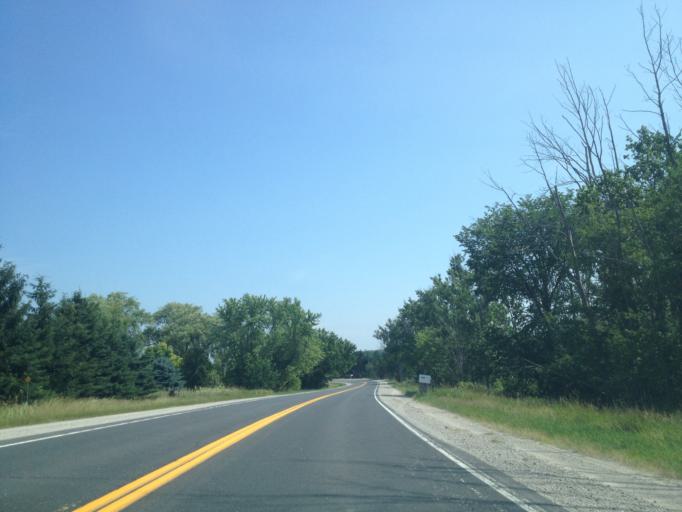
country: CA
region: Ontario
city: Huron East
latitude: 43.4009
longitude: -81.2226
